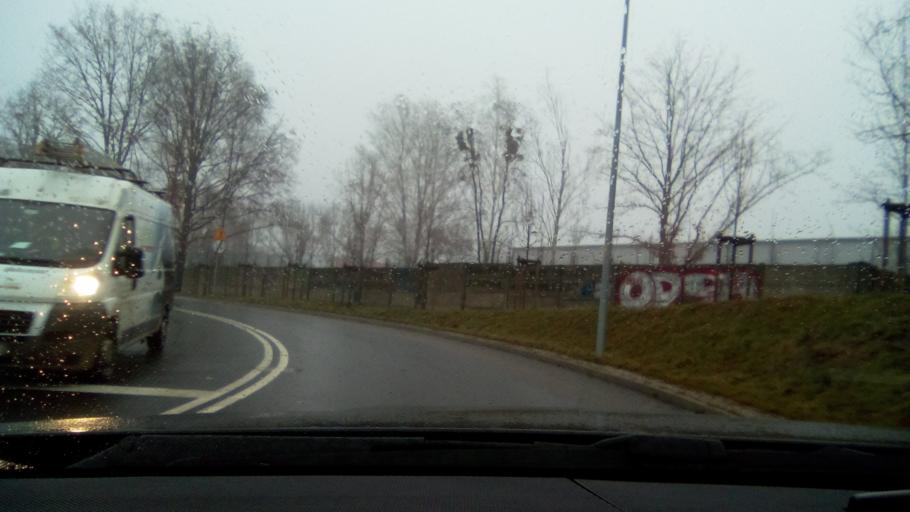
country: PL
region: Greater Poland Voivodeship
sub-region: Powiat poznanski
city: Swarzedz
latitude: 52.3882
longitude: 17.0095
